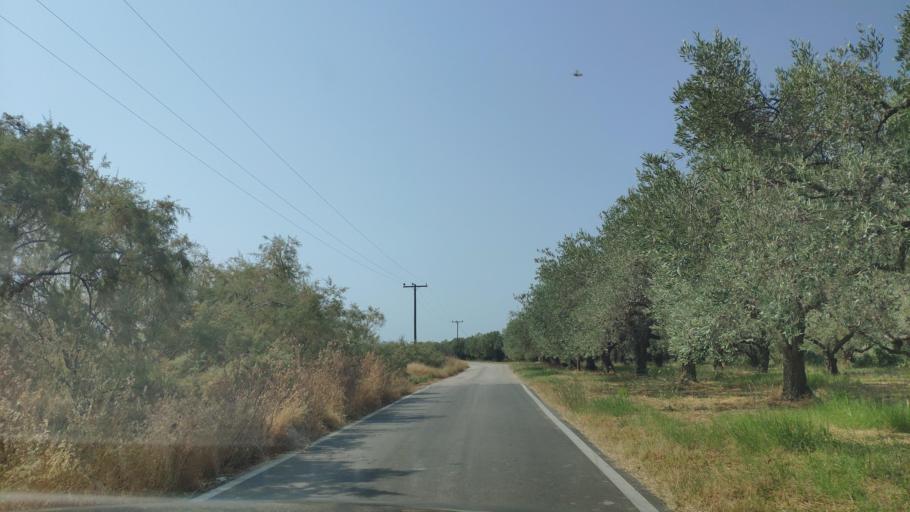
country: GR
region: West Greece
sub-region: Nomos Aitolias kai Akarnanias
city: Menidi
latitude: 39.0456
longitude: 21.0722
